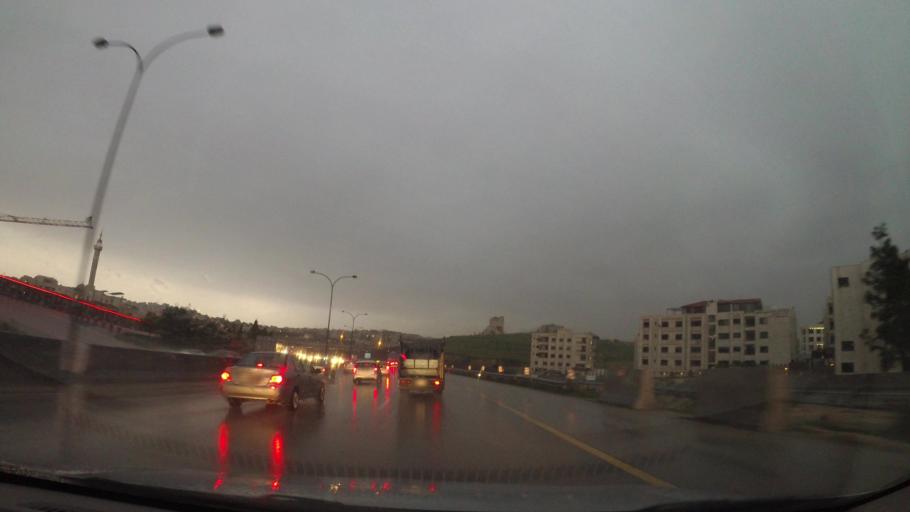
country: JO
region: Amman
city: Umm as Summaq
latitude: 31.9068
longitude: 35.8680
